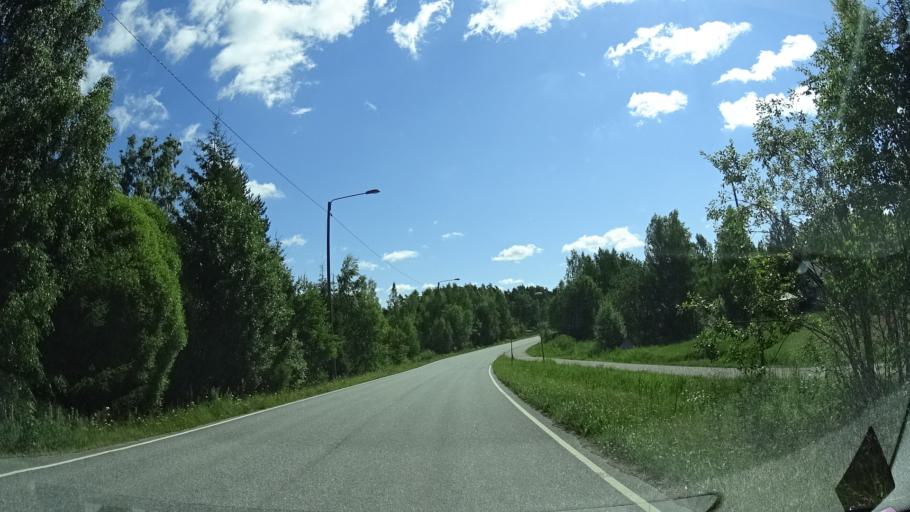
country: FI
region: Varsinais-Suomi
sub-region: Turku
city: Lemu
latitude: 60.5725
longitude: 21.9552
